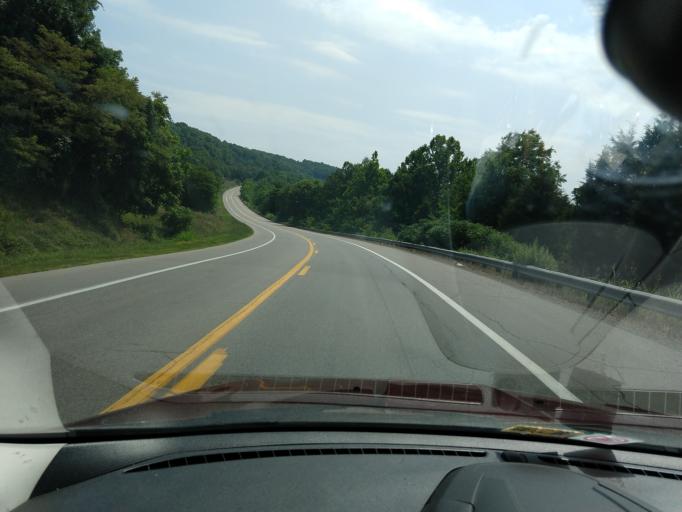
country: US
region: West Virginia
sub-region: Jackson County
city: Ravenswood
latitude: 38.8591
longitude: -81.8159
